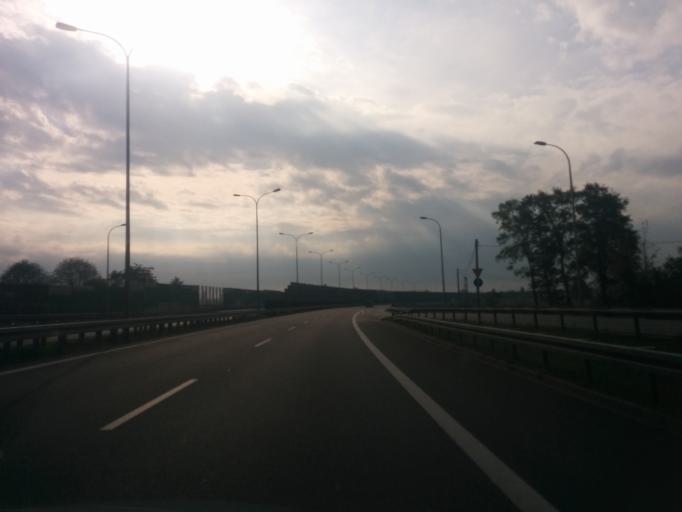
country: PL
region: Masovian Voivodeship
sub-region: Powiat bialobrzeski
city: Stara Blotnica
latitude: 51.5688
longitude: 21.0225
